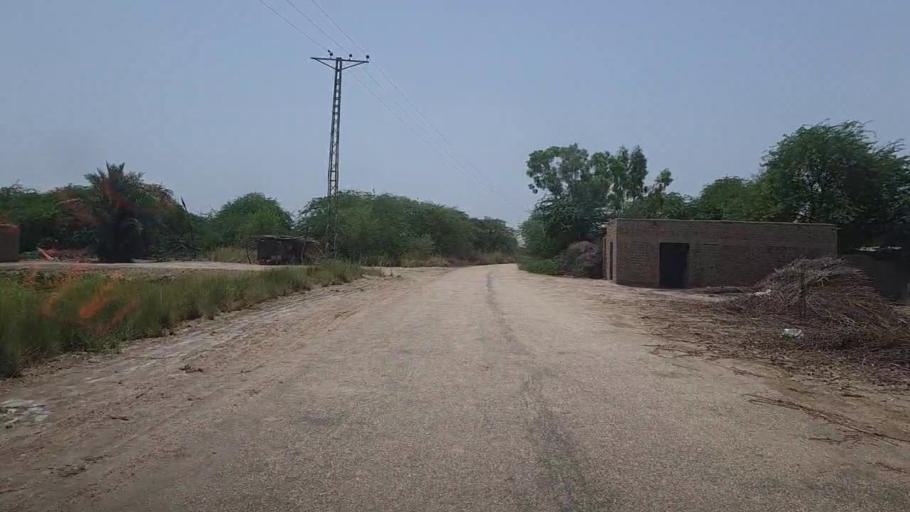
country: PK
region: Sindh
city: Pad Idan
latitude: 26.8343
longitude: 68.3244
